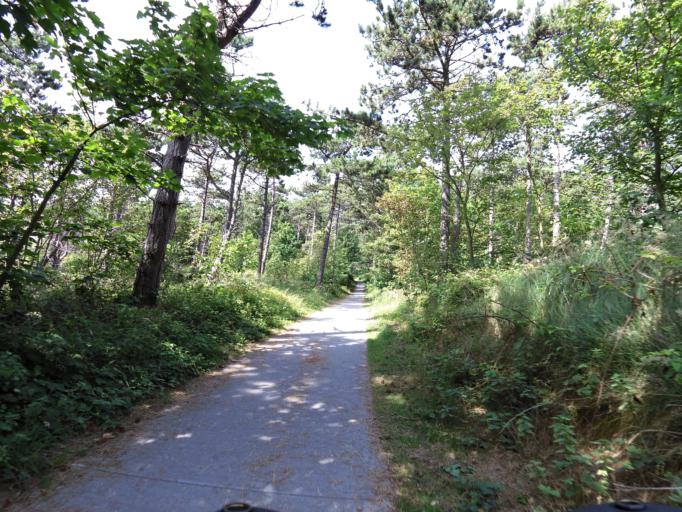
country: NL
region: Zeeland
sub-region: Schouwen-Duiveland
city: Burgh
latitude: 51.6790
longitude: 3.6938
